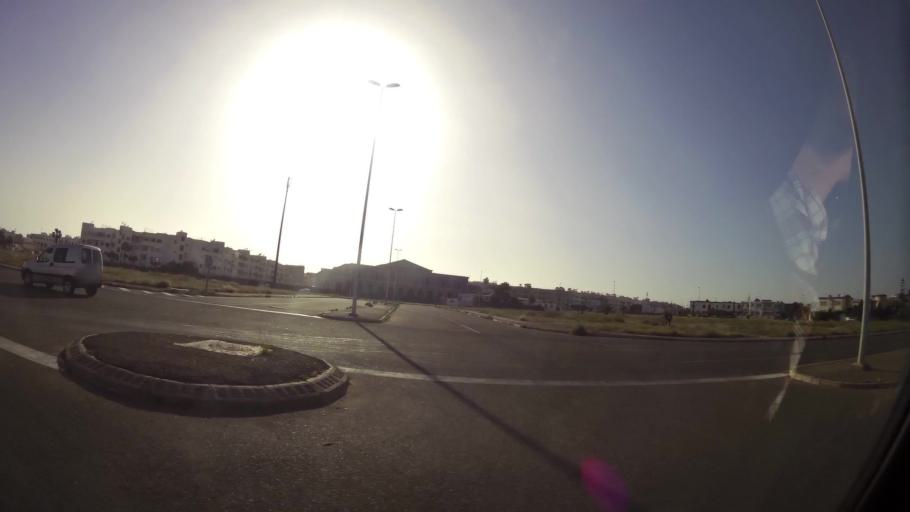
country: MA
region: Oued ed Dahab-Lagouira
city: Dakhla
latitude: 30.4000
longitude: -9.5412
